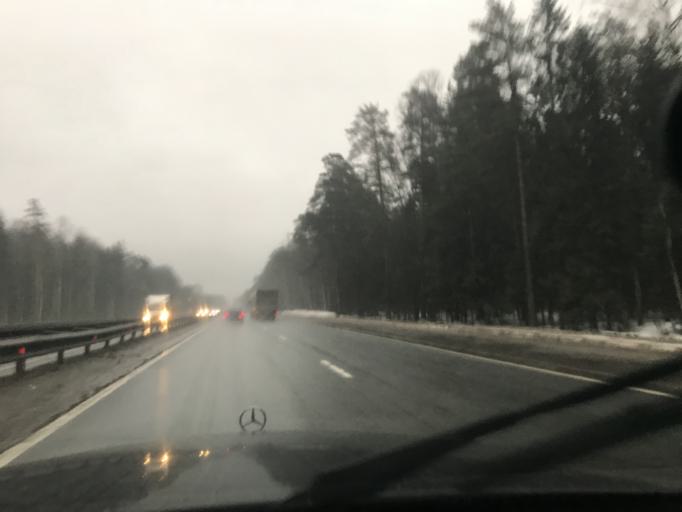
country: RU
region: Vladimir
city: Stepantsevo
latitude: 56.2279
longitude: 41.6795
